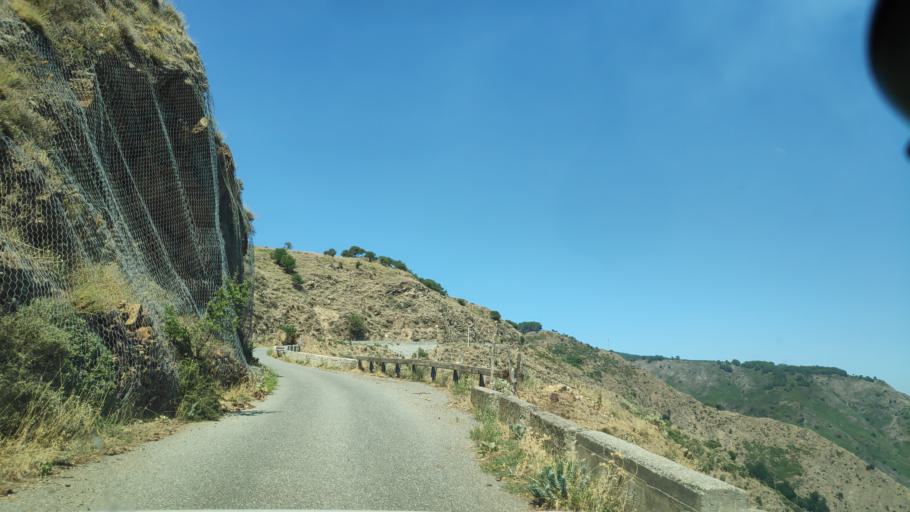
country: IT
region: Calabria
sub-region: Provincia di Reggio Calabria
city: Bova
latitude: 38.0090
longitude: 15.9327
